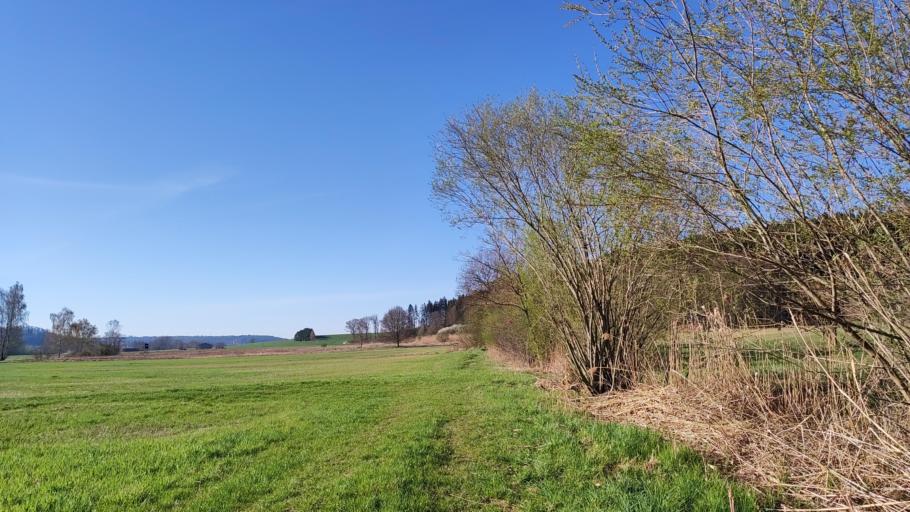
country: DE
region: Bavaria
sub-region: Swabia
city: Altenmunster
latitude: 48.4323
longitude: 10.5885
